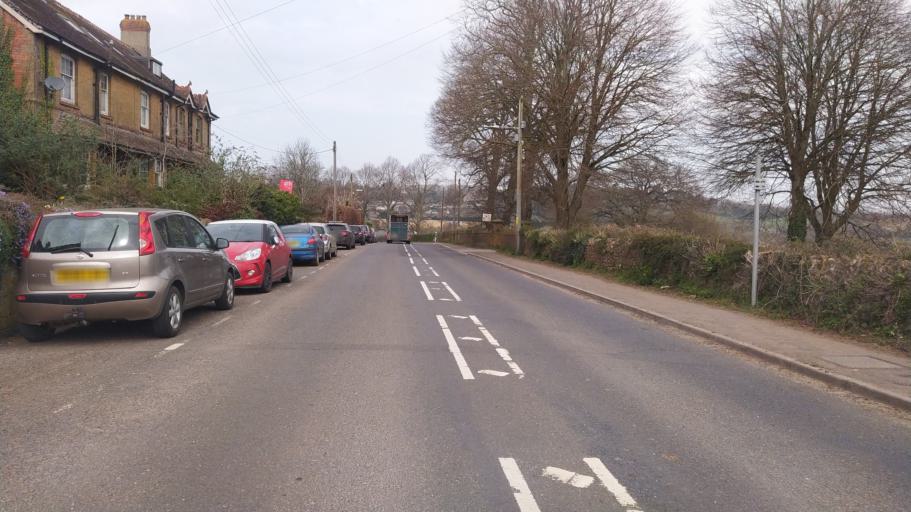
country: GB
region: England
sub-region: Somerset
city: Crewkerne
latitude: 50.8777
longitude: -2.7805
